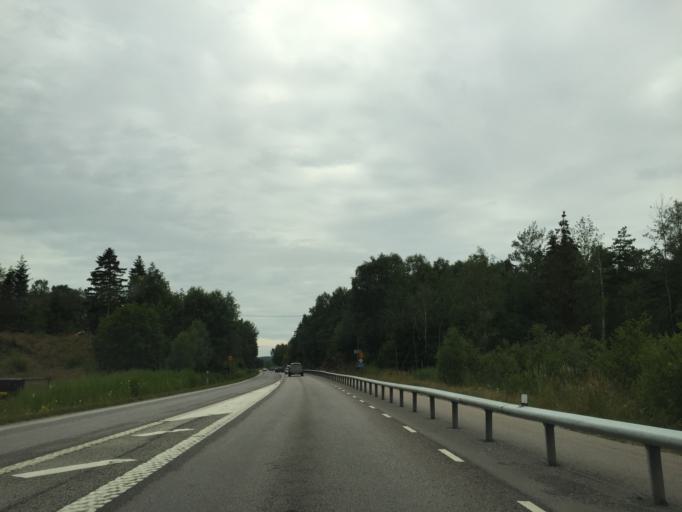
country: SE
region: Vaestra Goetaland
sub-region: Tjorns Kommun
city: Myggenas
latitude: 58.0382
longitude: 11.7331
